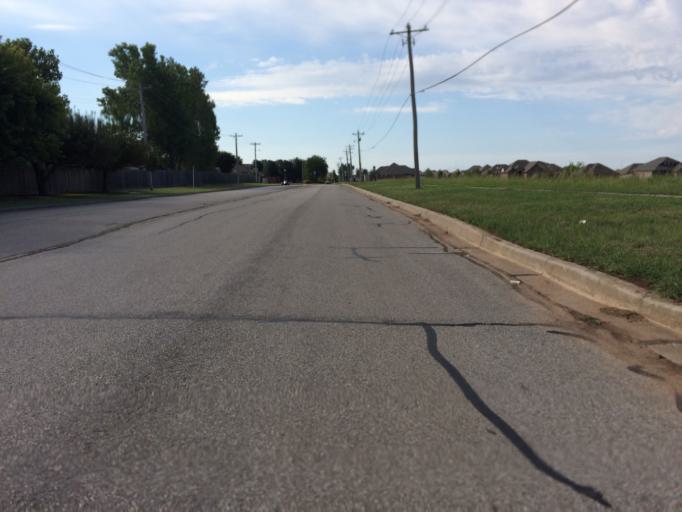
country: US
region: Oklahoma
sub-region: Cleveland County
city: Noble
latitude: 35.1858
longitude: -97.4059
